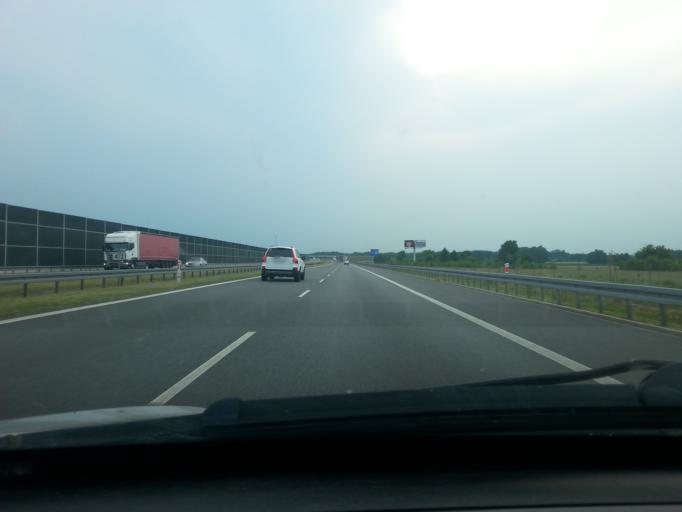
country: PL
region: Lodz Voivodeship
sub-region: Powiat skierniewicki
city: Bolimow
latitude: 52.0749
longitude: 20.2541
